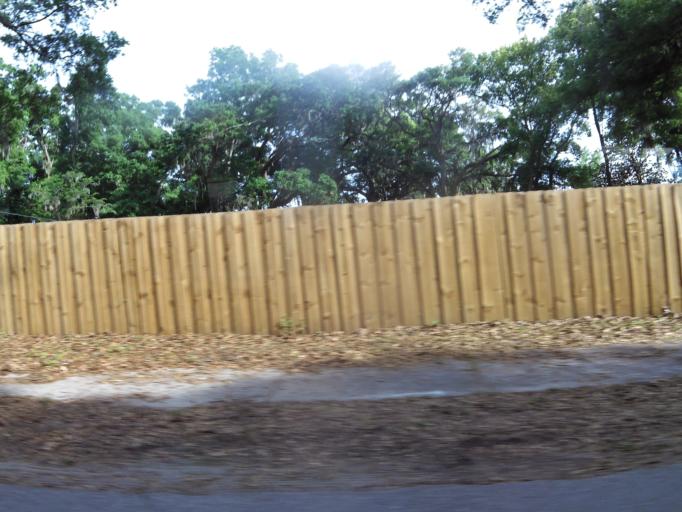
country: US
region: Florida
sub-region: Duval County
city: Jacksonville
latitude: 30.3301
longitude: -81.5960
